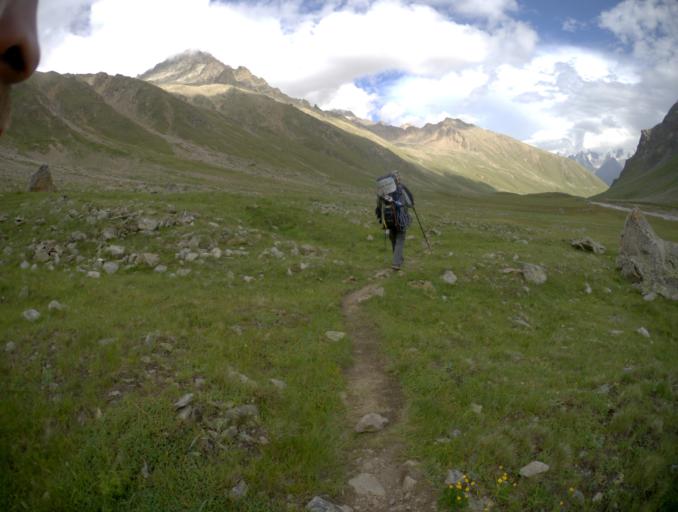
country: RU
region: Kabardino-Balkariya
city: Terskol
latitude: 43.3218
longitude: 42.5742
